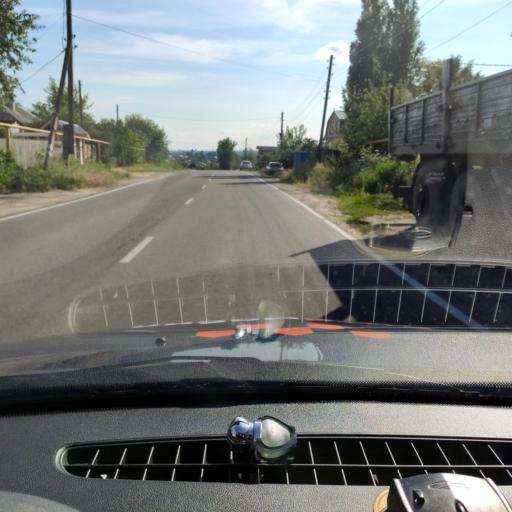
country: RU
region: Voronezj
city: Devitsa
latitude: 51.6479
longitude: 38.9690
